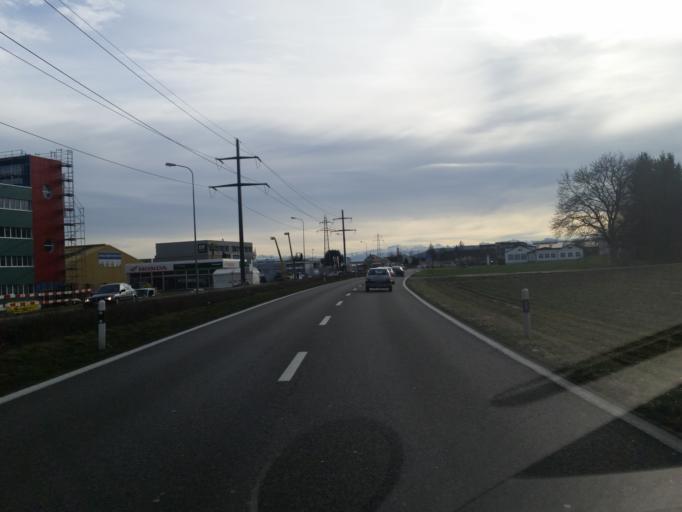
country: CH
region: Aargau
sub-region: Bezirk Bremgarten
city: Dottikon
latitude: 47.3728
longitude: 8.2281
